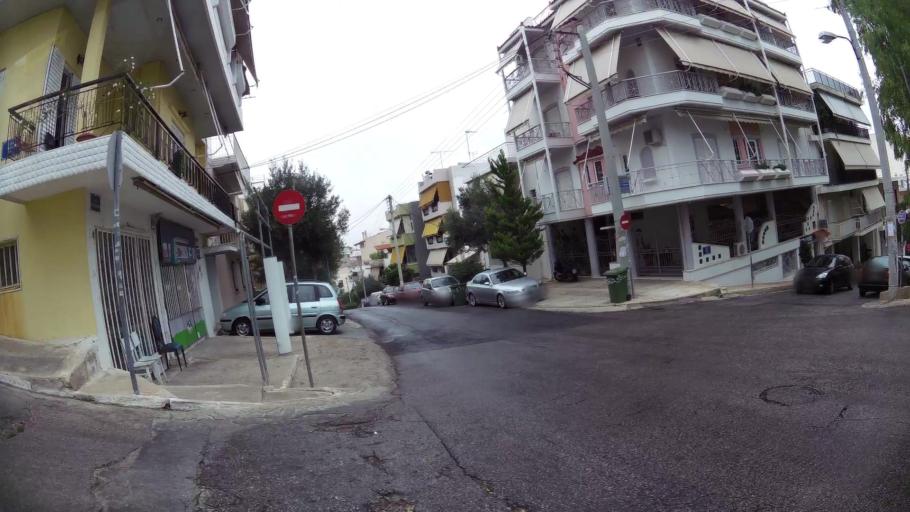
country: GR
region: Attica
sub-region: Nomos Piraios
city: Korydallos
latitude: 37.9881
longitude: 23.6472
